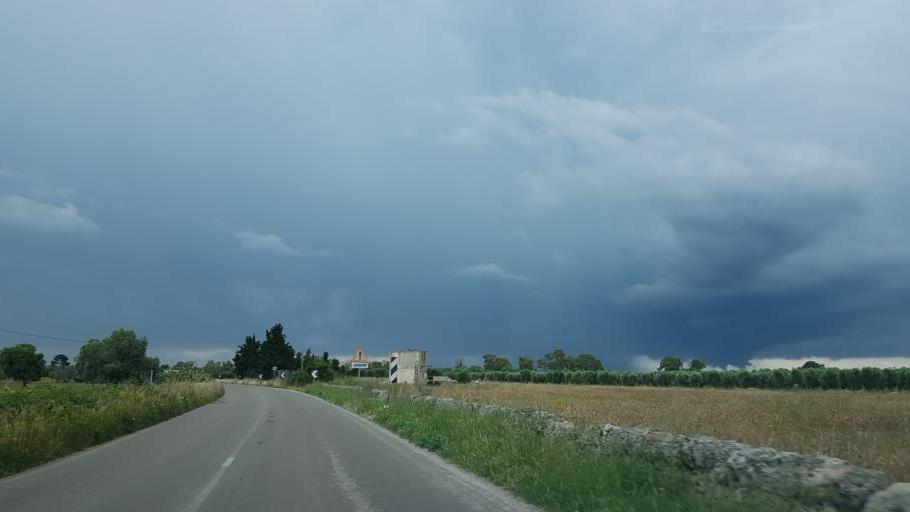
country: IT
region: Apulia
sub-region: Provincia di Lecce
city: Porto Cesareo
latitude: 40.3075
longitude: 17.8628
